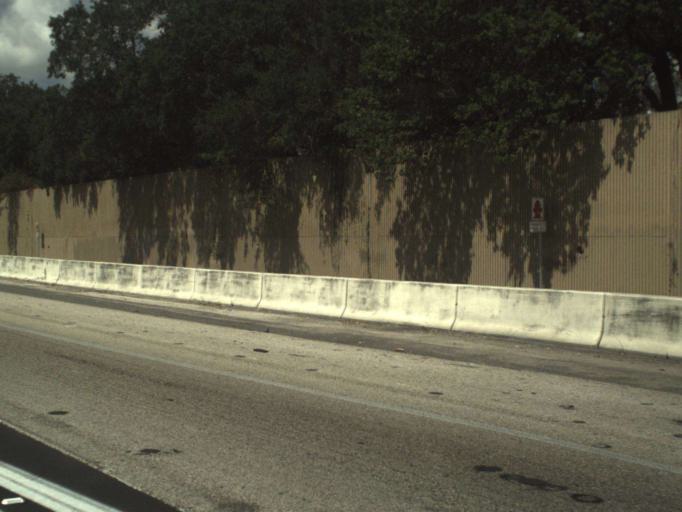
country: US
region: Florida
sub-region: Broward County
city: Hollywood
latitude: 26.0288
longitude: -80.1658
